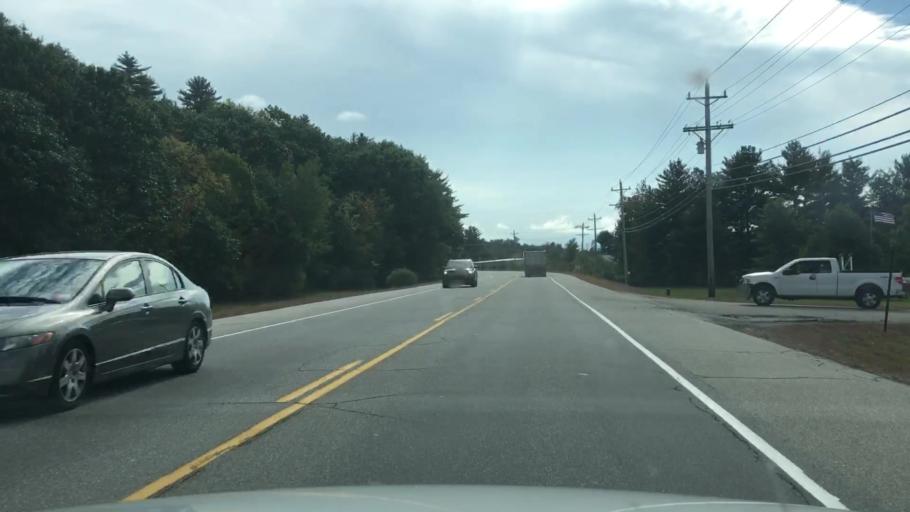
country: US
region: New Hampshire
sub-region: Carroll County
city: North Conway
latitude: 44.0897
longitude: -71.1487
